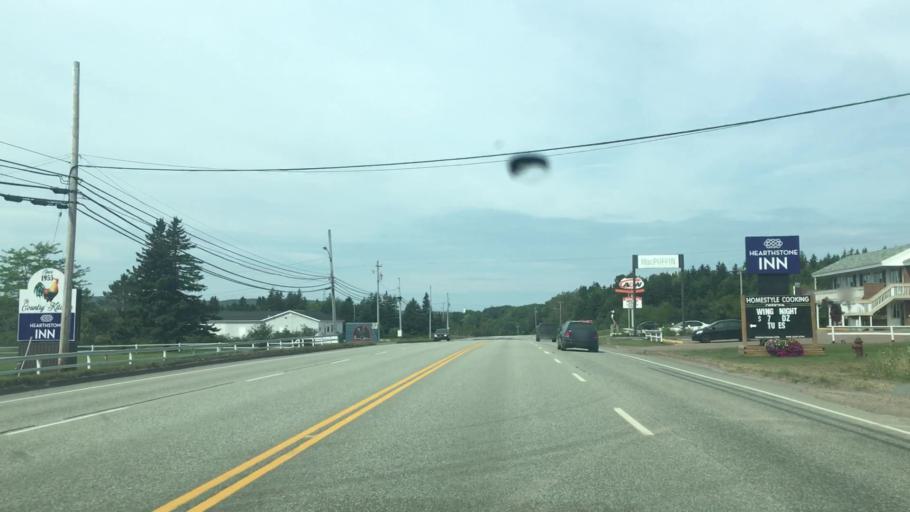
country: CA
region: Nova Scotia
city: Port Hawkesbury
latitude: 45.6412
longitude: -61.3892
